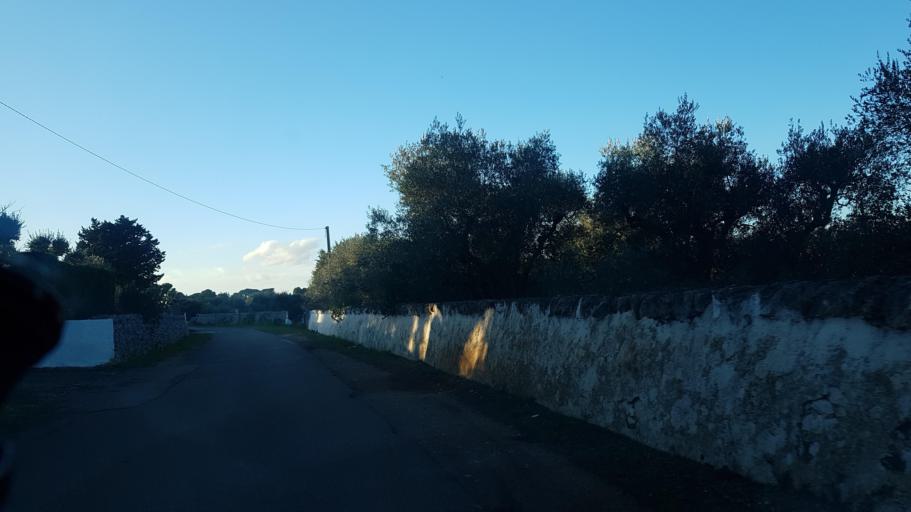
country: IT
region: Apulia
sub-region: Provincia di Brindisi
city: Ostuni
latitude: 40.7024
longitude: 17.5424
